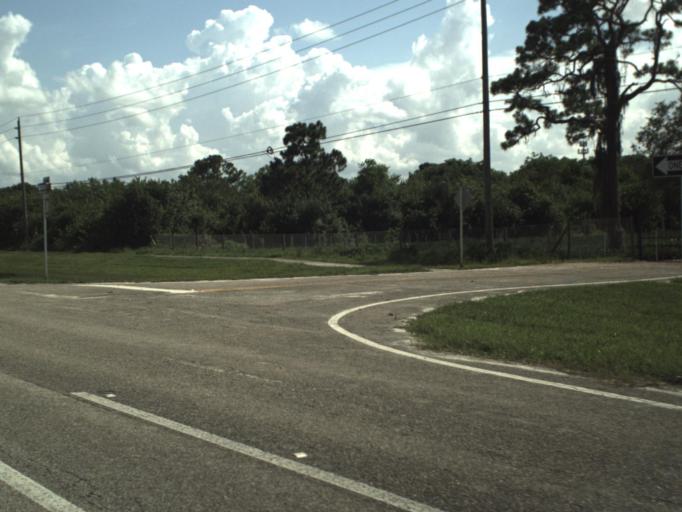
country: US
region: Florida
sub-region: Palm Beach County
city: Villages of Oriole
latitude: 26.4924
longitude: -80.2051
